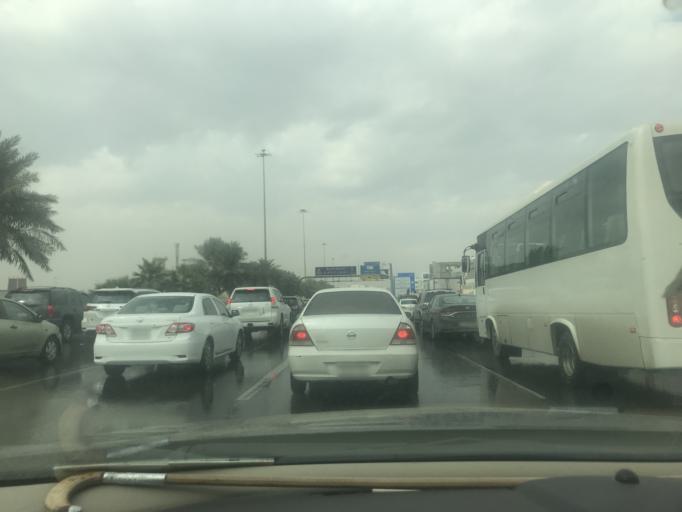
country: SA
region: Ar Riyad
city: Riyadh
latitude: 24.7077
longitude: 46.7668
